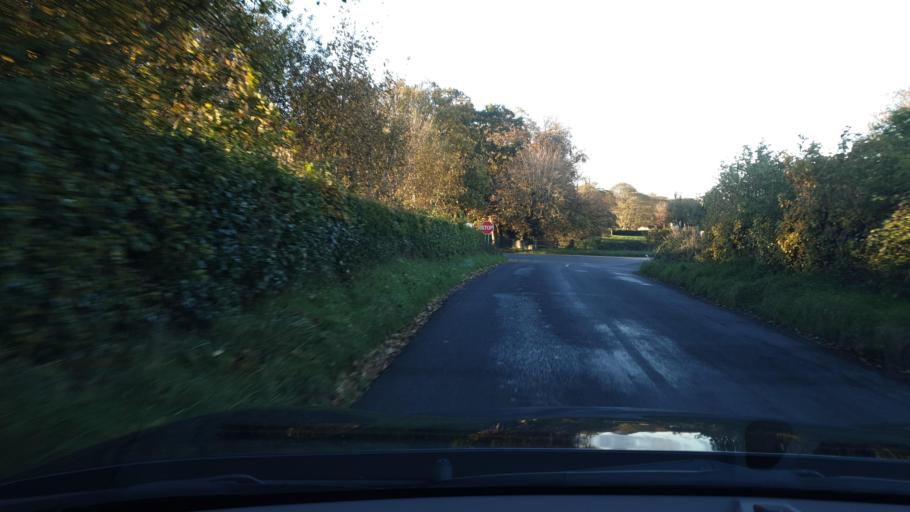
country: IE
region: Leinster
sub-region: Lu
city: Drogheda
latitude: 53.6918
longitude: -6.3431
